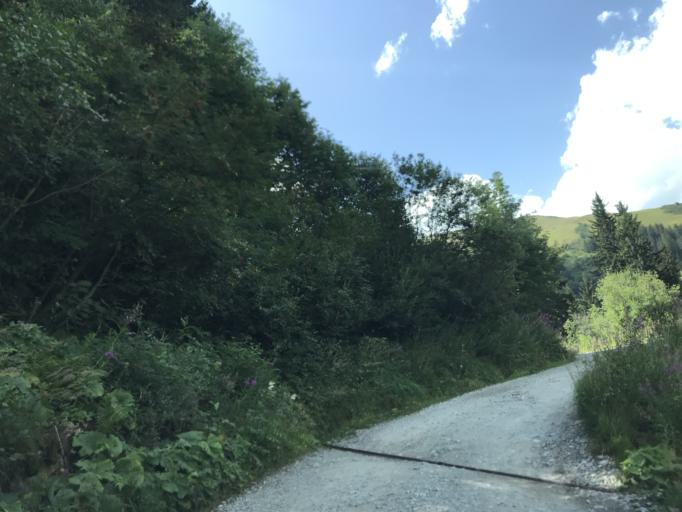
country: FR
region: Rhone-Alpes
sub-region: Departement de la Savoie
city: Beaufort
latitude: 45.6658
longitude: 6.6165
